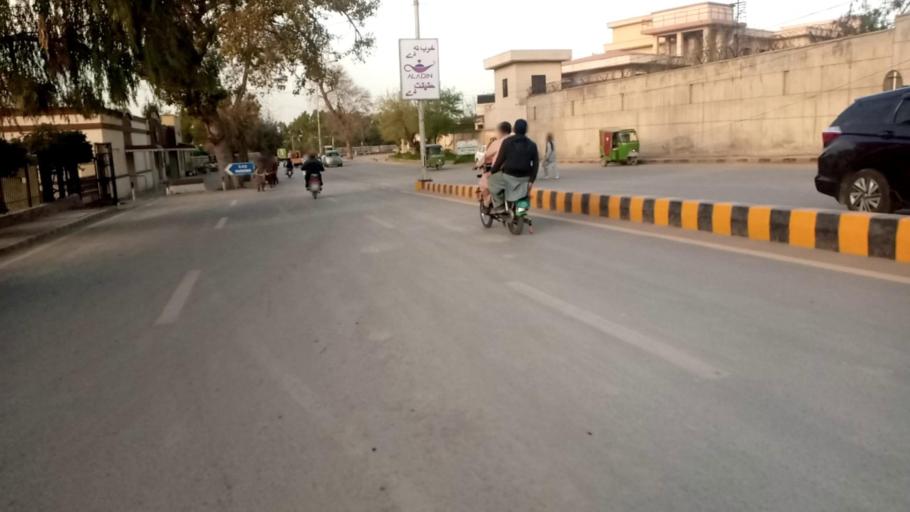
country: PK
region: Khyber Pakhtunkhwa
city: Peshawar
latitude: 34.0148
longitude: 71.5520
